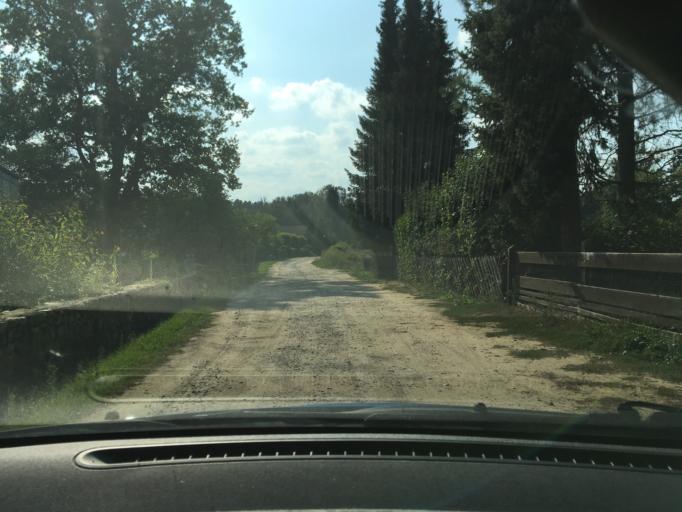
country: DE
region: Lower Saxony
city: Soderstorf
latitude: 53.1431
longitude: 10.1658
